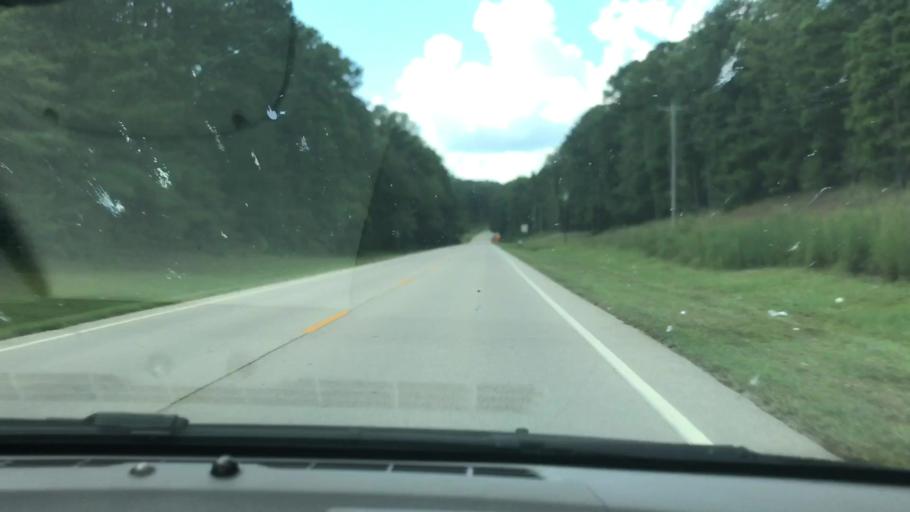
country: US
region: Georgia
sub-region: Troup County
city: La Grange
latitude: 33.1003
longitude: -85.0661
